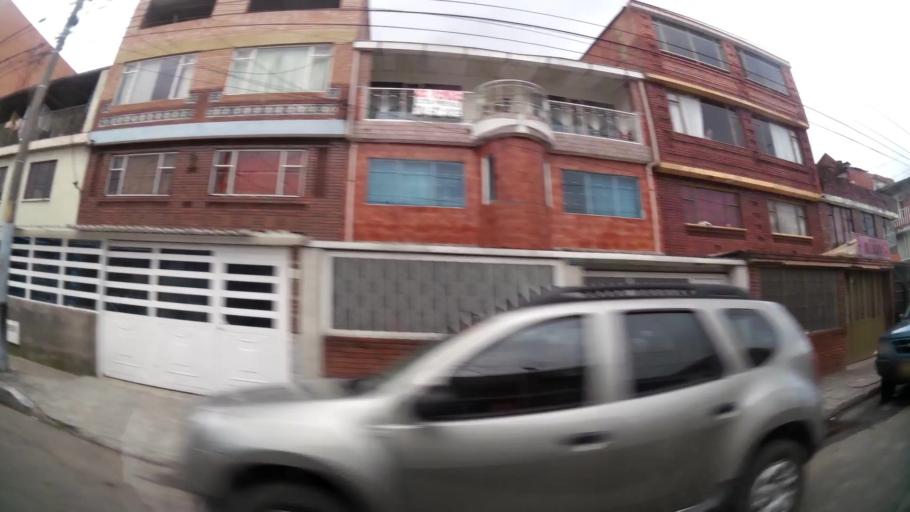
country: CO
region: Bogota D.C.
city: Bogota
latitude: 4.6881
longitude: -74.1040
